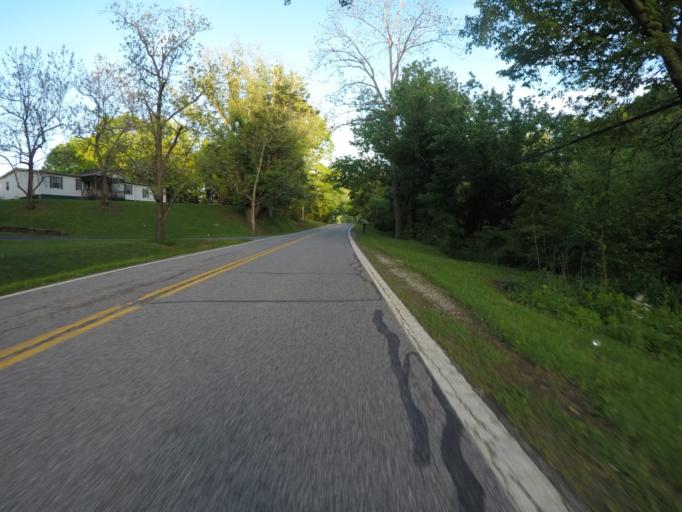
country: US
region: West Virginia
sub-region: Cabell County
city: Huntington
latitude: 38.4894
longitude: -82.4756
